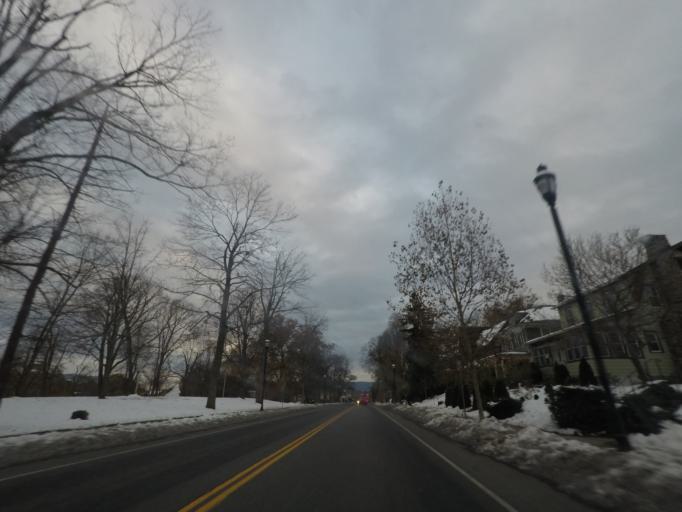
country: US
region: New York
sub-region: Orange County
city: Newburgh
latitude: 41.5071
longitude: -74.0206
